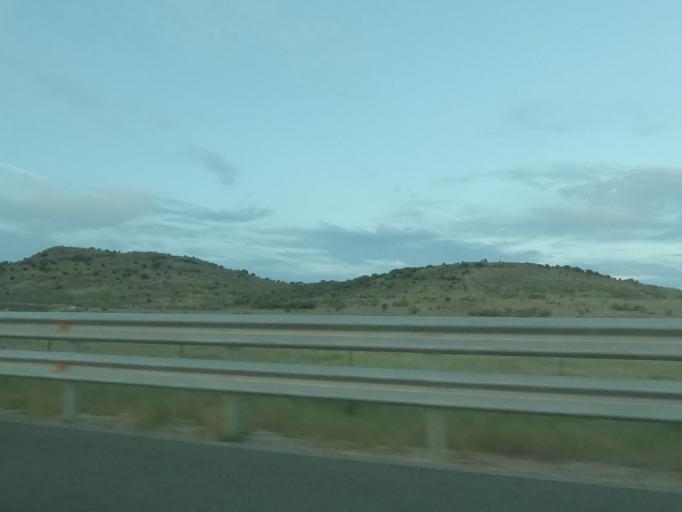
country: ES
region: Extremadura
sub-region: Provincia de Caceres
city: Caceres
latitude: 39.4237
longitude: -6.4021
